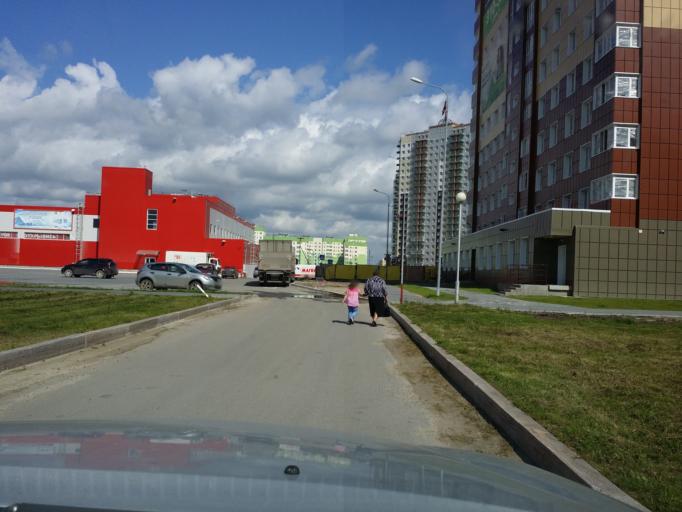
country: RU
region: Khanty-Mansiyskiy Avtonomnyy Okrug
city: Nizhnevartovsk
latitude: 60.9280
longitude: 76.6087
